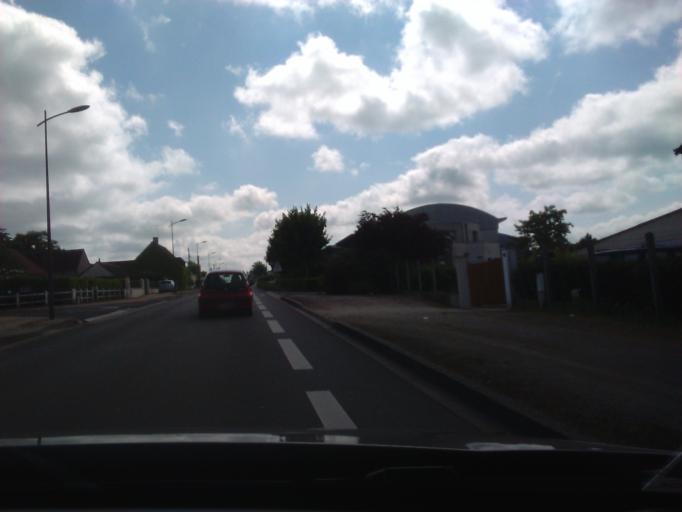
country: FR
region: Centre
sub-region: Departement du Loir-et-Cher
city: Vendome
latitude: 47.7824
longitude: 1.0657
